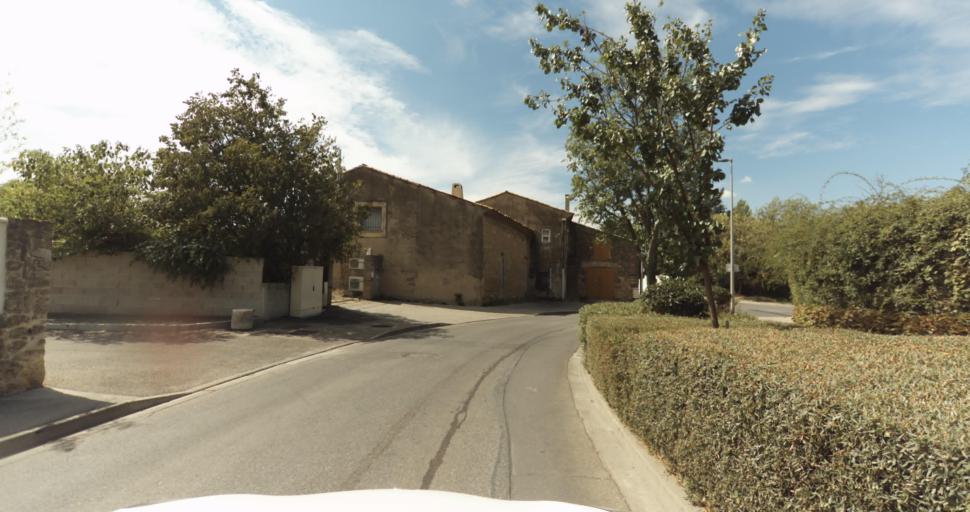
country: FR
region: Provence-Alpes-Cote d'Azur
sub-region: Departement des Bouches-du-Rhone
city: Miramas
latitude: 43.5818
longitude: 5.0145
